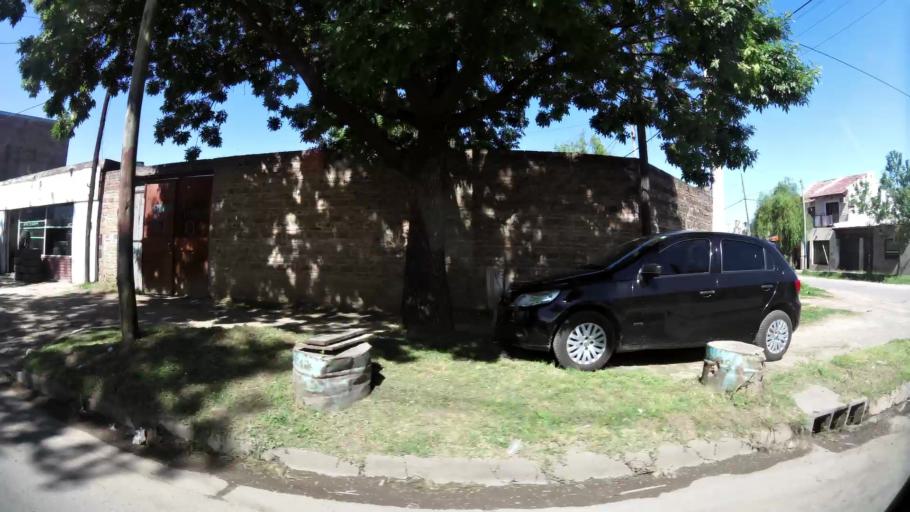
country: AR
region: Santa Fe
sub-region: Departamento de Rosario
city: Rosario
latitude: -32.9280
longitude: -60.7039
